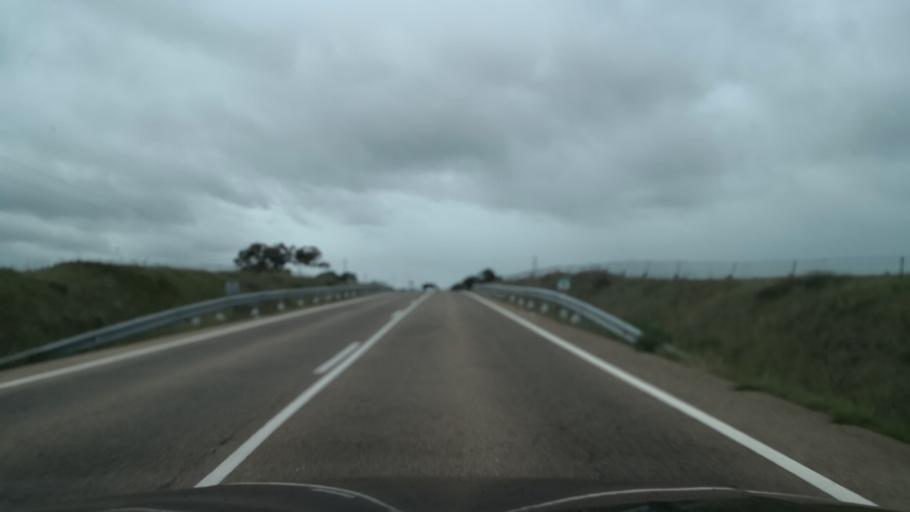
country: ES
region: Extremadura
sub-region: Provincia de Badajoz
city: Badajoz
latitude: 38.9695
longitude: -6.8946
